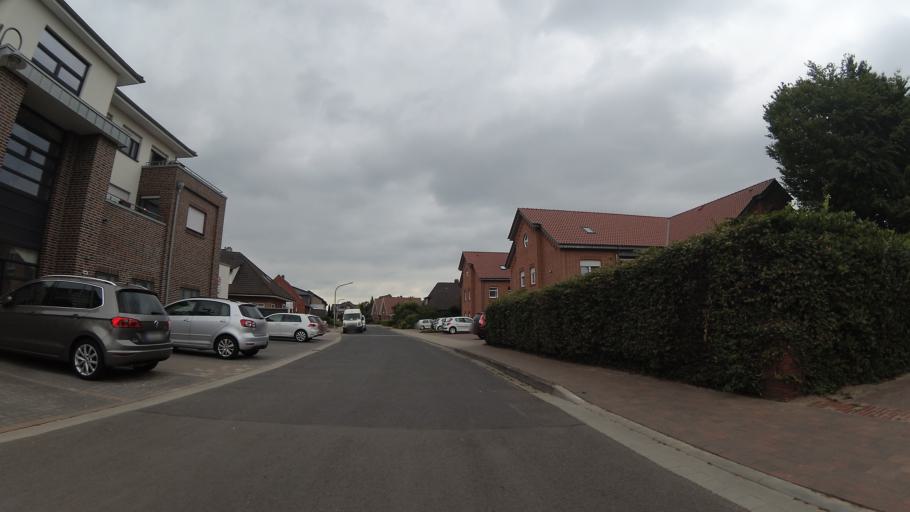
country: DE
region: Lower Saxony
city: Lathen
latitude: 52.8617
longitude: 7.3184
